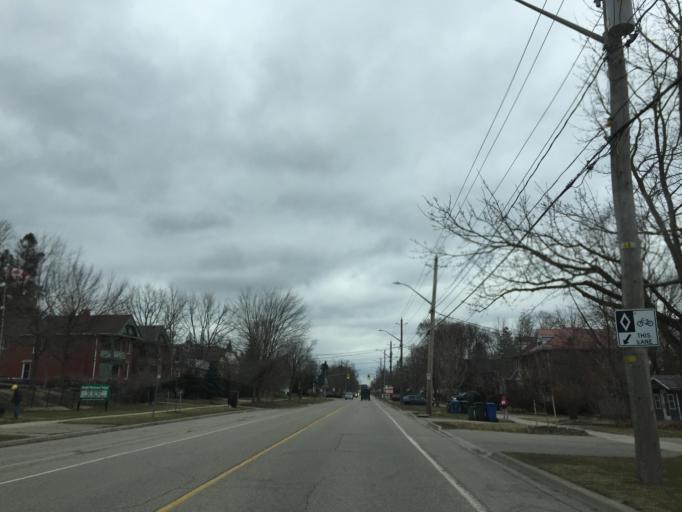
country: CA
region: Ontario
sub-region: Wellington County
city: Guelph
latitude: 43.5368
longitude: -80.2544
